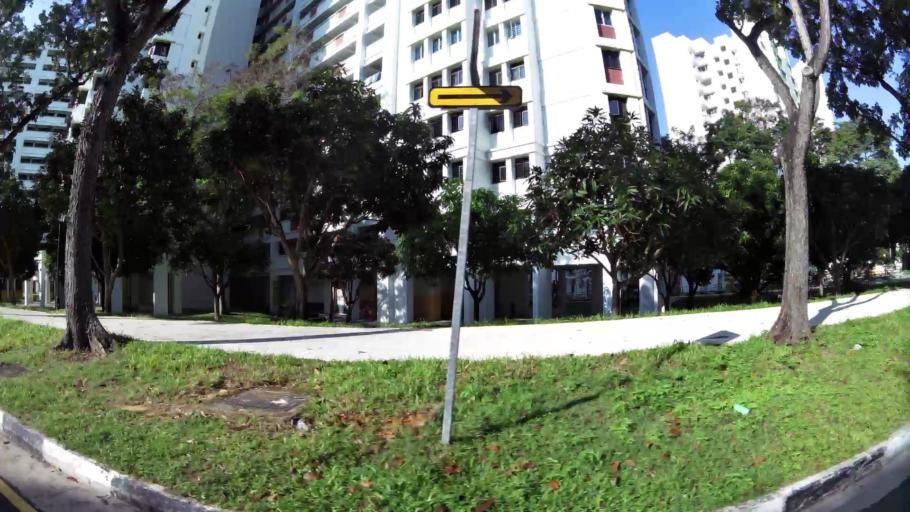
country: SG
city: Singapore
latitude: 1.3278
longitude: 103.9248
